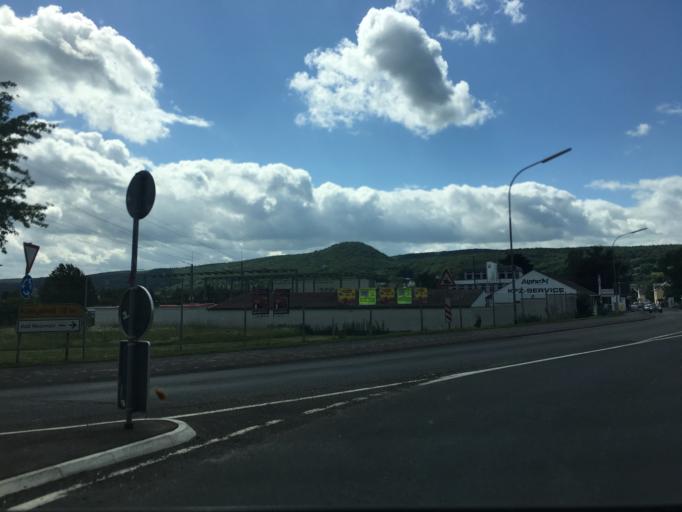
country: DE
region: Rheinland-Pfalz
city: Bad Neuenahr-Ahrweiler
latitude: 50.5505
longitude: 7.1193
